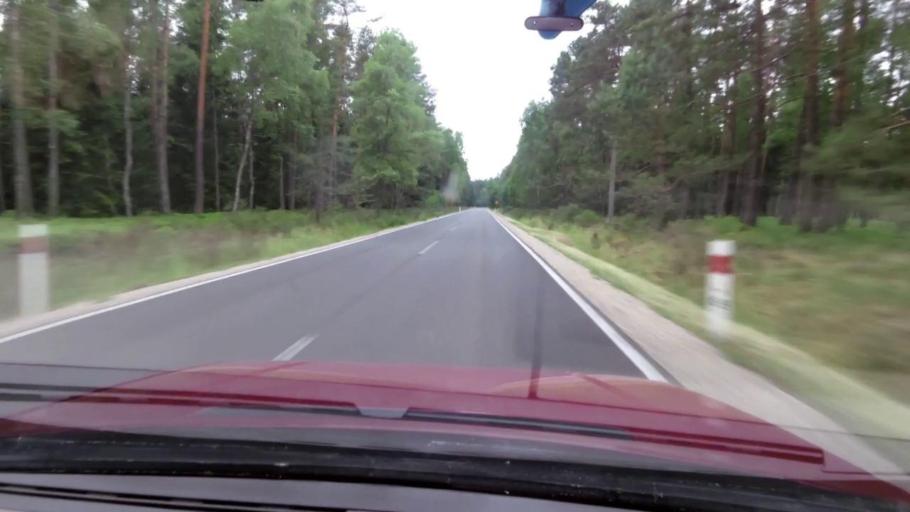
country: PL
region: West Pomeranian Voivodeship
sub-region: Powiat koszalinski
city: Sianow
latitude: 54.1478
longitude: 16.4753
